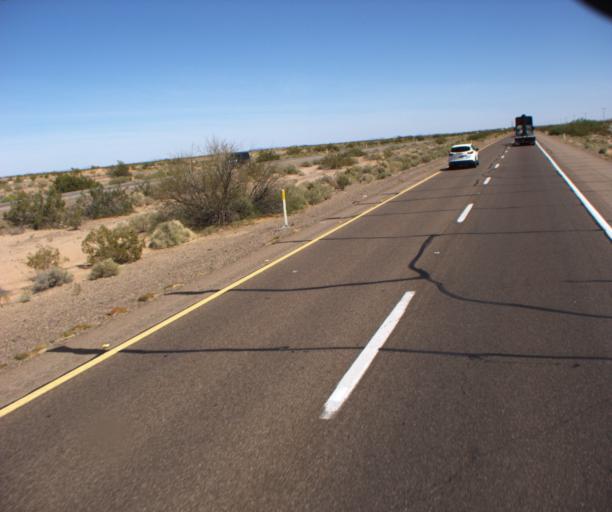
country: US
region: Arizona
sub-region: Yuma County
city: Wellton
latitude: 32.7756
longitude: -113.5961
